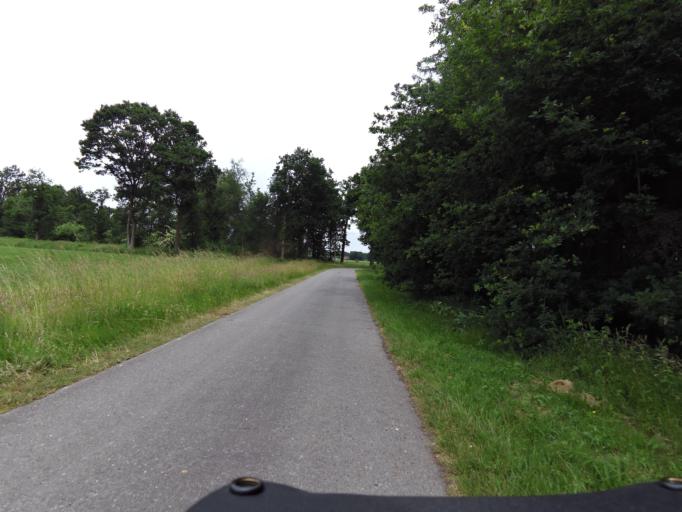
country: NL
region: North Brabant
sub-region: Gemeente Goirle
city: Goirle
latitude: 51.4491
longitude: 5.0613
